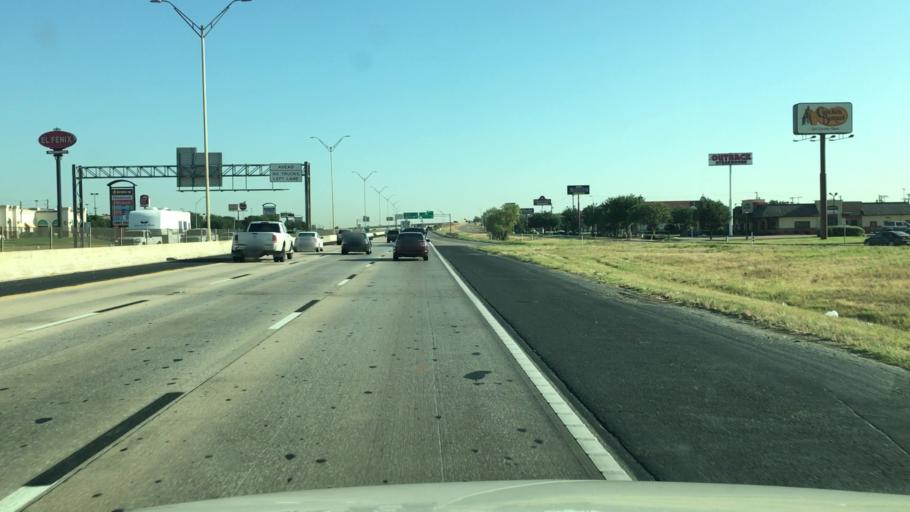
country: US
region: Texas
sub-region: Johnson County
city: Burleson
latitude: 32.5646
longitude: -97.3188
